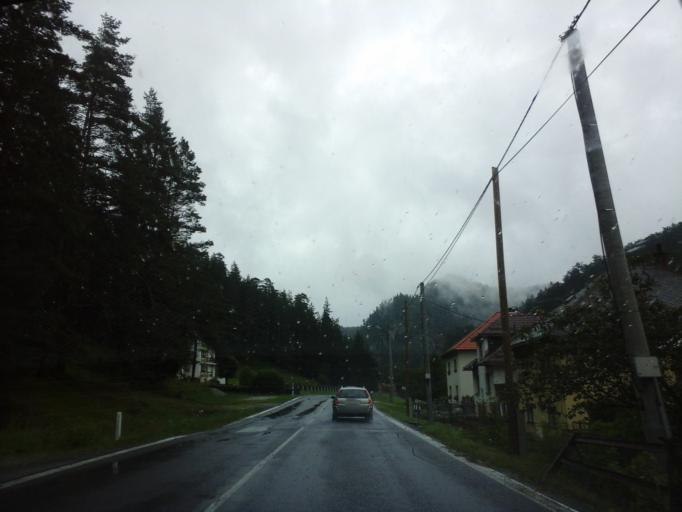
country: SK
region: Presovsky
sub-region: Okres Poprad
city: Poprad
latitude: 48.9261
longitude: 20.2781
